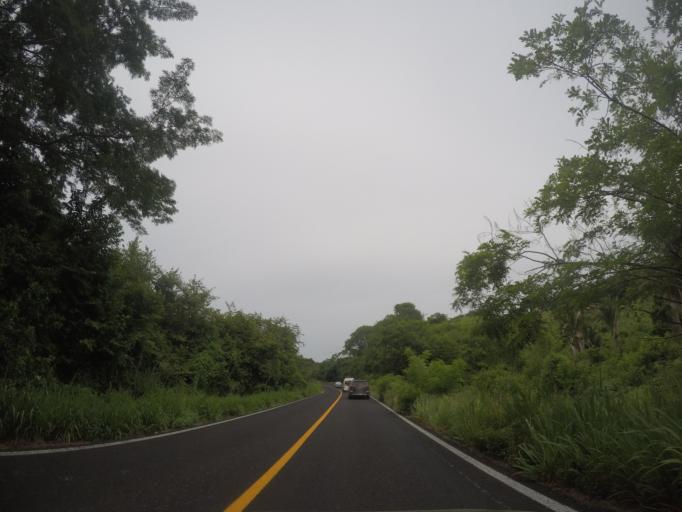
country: MX
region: Oaxaca
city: San Pedro Mixtepec
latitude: 15.9512
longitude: -97.2738
